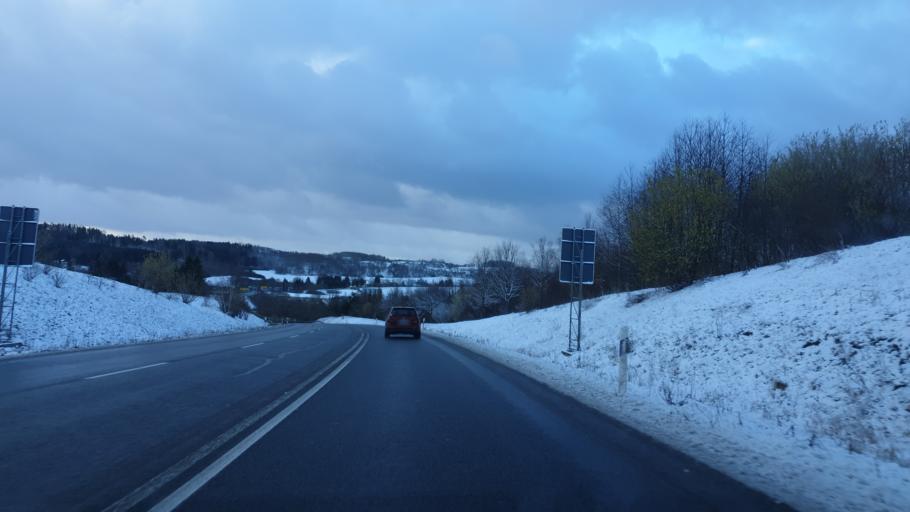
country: DE
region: Saxony
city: Oelsnitz
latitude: 50.4216
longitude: 12.1473
